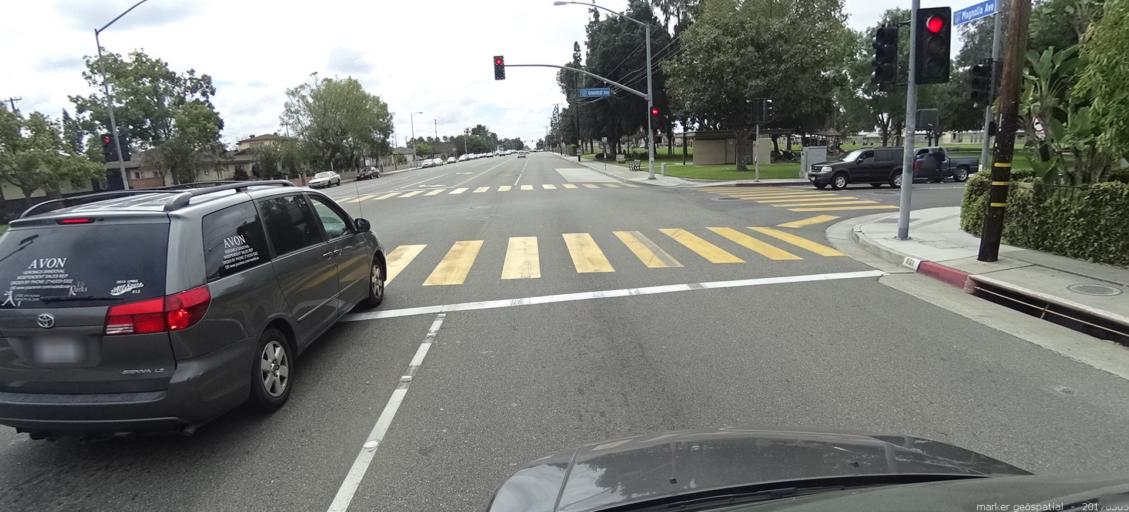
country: US
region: California
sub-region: Orange County
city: Buena Park
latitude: 33.8426
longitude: -117.9762
